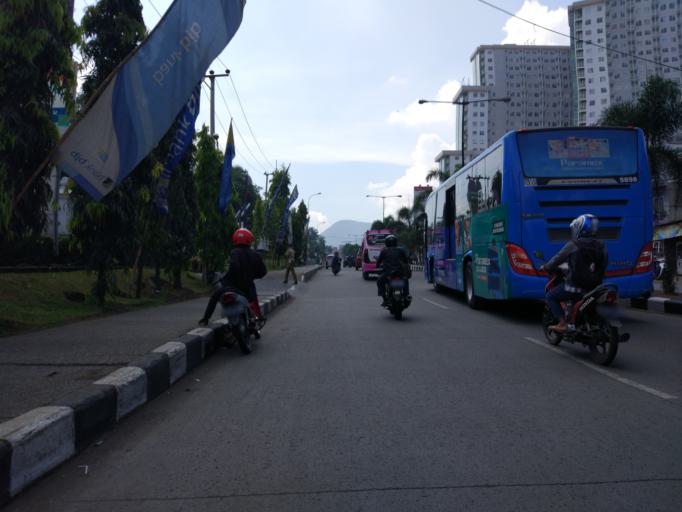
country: ID
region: West Java
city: Cileunyi
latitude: -6.9362
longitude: 107.7633
